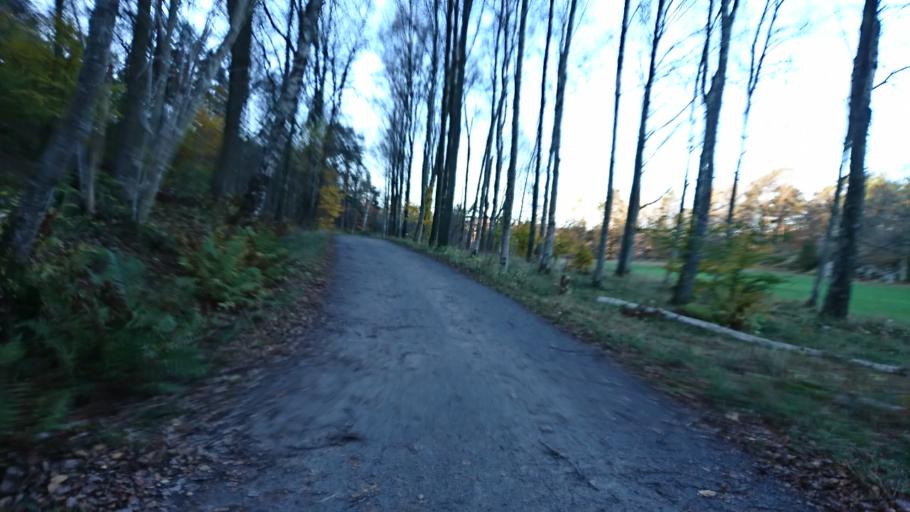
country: SE
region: Vaestra Goetaland
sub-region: Molndal
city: Moelndal
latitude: 57.6901
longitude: 12.0293
